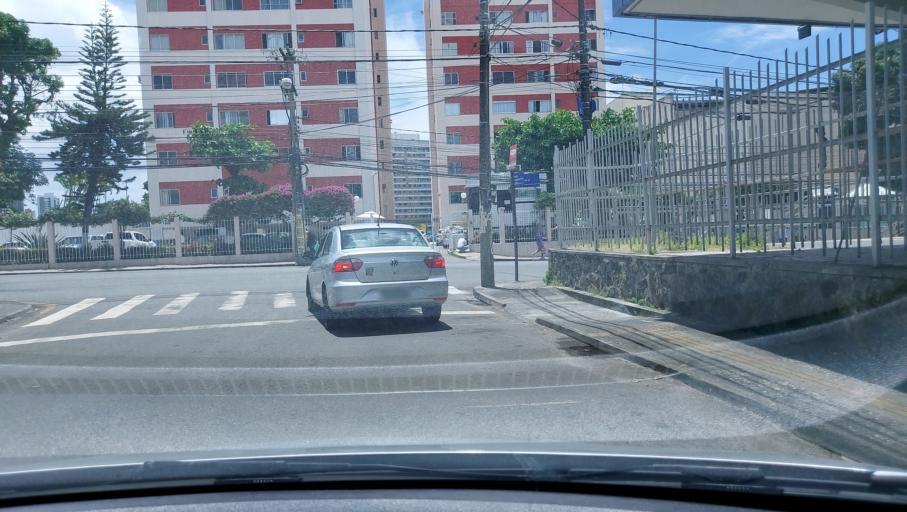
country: BR
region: Bahia
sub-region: Salvador
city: Salvador
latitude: -12.9896
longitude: -38.4904
